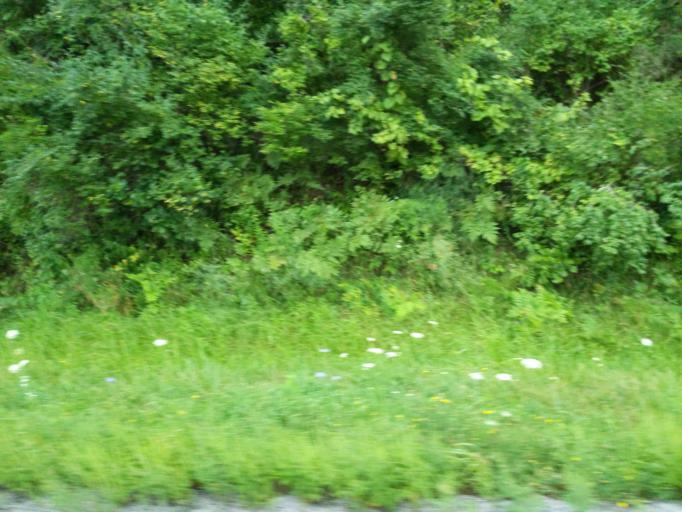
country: US
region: Wisconsin
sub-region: Sauk County
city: Sauk City
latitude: 43.2428
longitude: -89.7264
